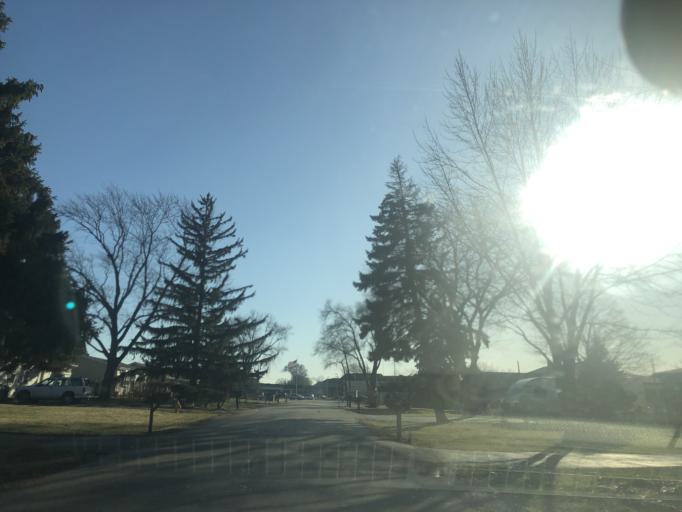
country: US
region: Illinois
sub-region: DuPage County
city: Addison
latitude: 41.9407
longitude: -88.0048
